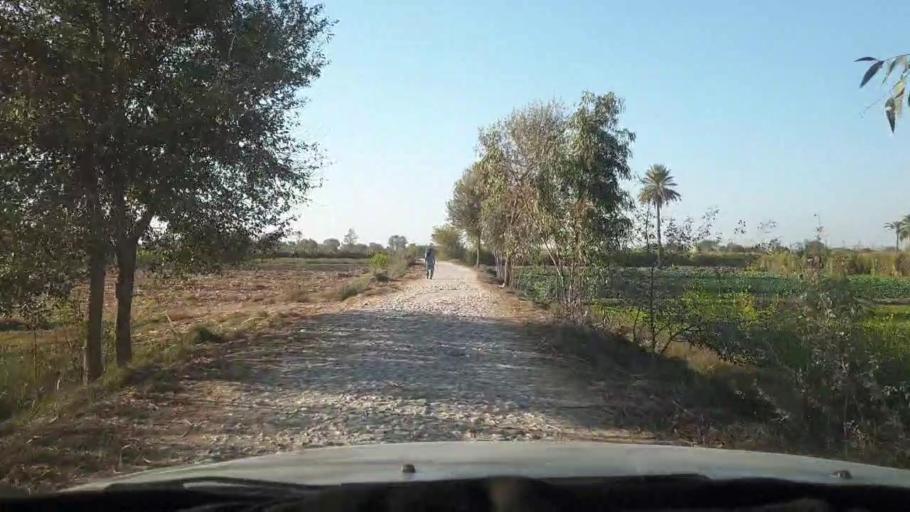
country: PK
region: Sindh
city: Adilpur
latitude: 27.9514
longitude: 69.2334
